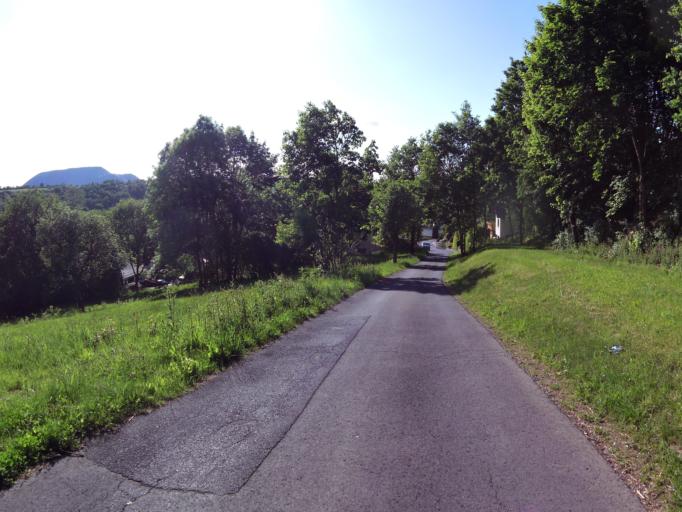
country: DE
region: Thuringia
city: Vacha
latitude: 50.8348
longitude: 10.0188
